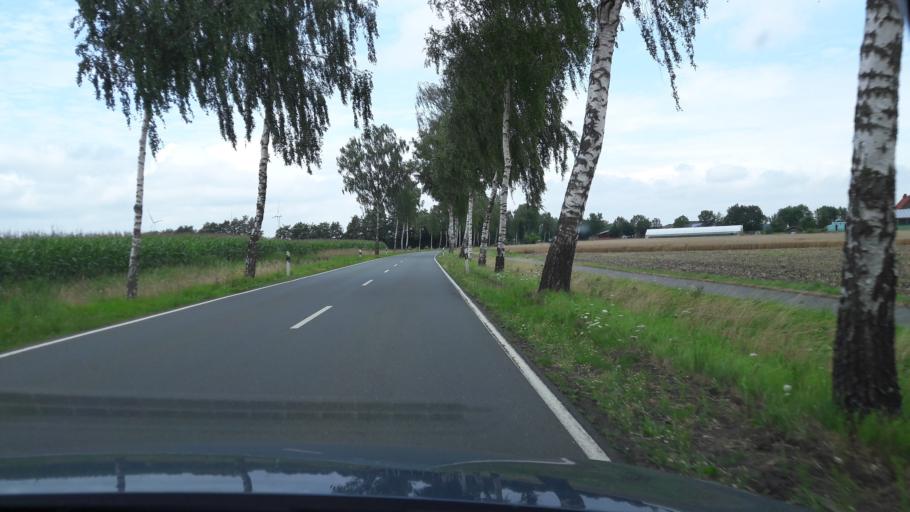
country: DE
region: North Rhine-Westphalia
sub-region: Regierungsbezirk Munster
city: Everswinkel
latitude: 51.8828
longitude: 7.8932
